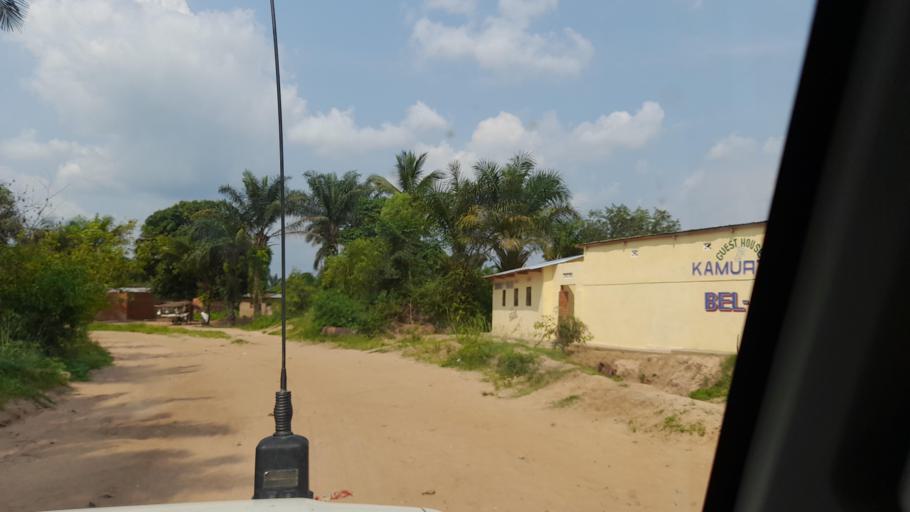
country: CD
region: Kasai-Occidental
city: Kananga
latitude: -5.9159
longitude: 22.4784
